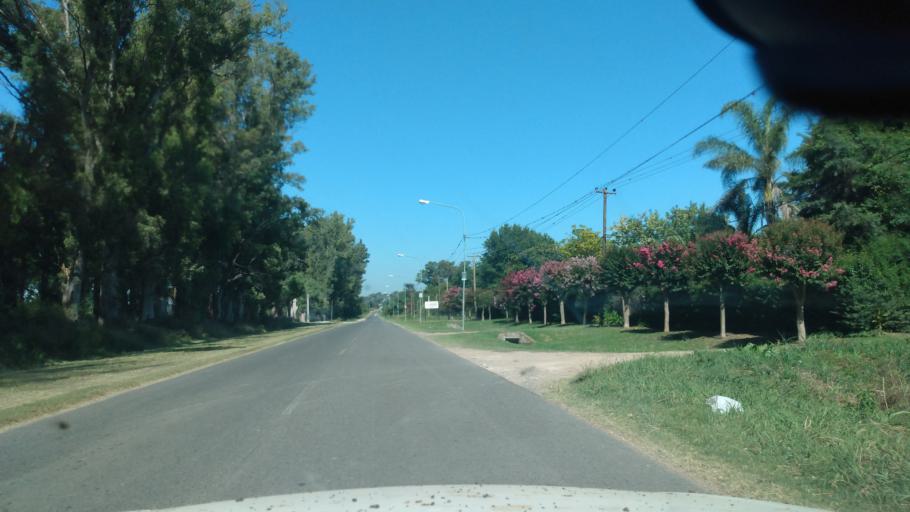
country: AR
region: Buenos Aires
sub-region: Partido de Lujan
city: Lujan
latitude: -34.5056
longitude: -59.0783
